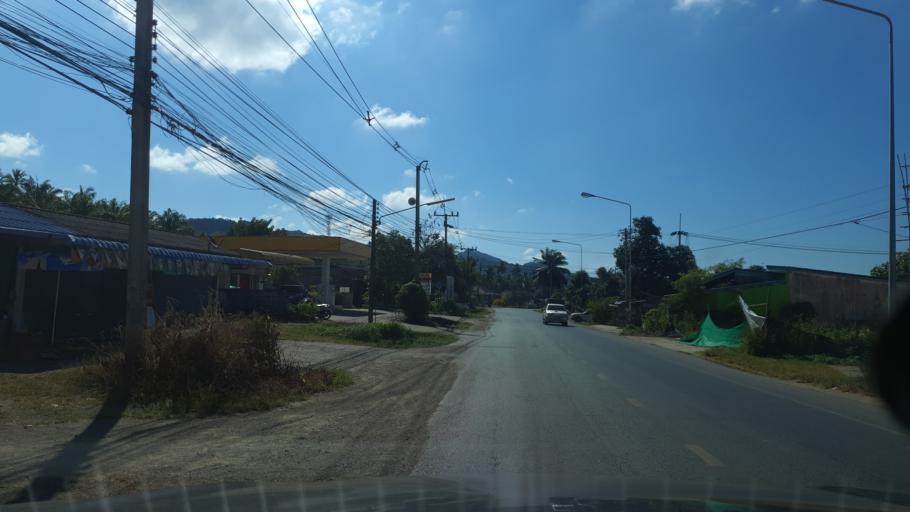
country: TH
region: Phangnga
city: Ban Ao Nang
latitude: 8.0598
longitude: 98.8138
